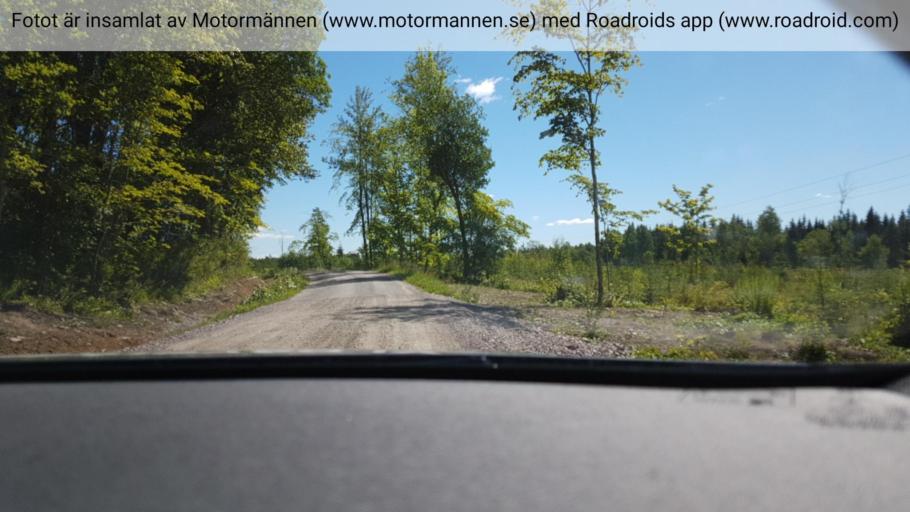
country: SE
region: Vaestra Goetaland
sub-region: Falkopings Kommun
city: Akarp
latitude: 58.1865
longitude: 13.7763
